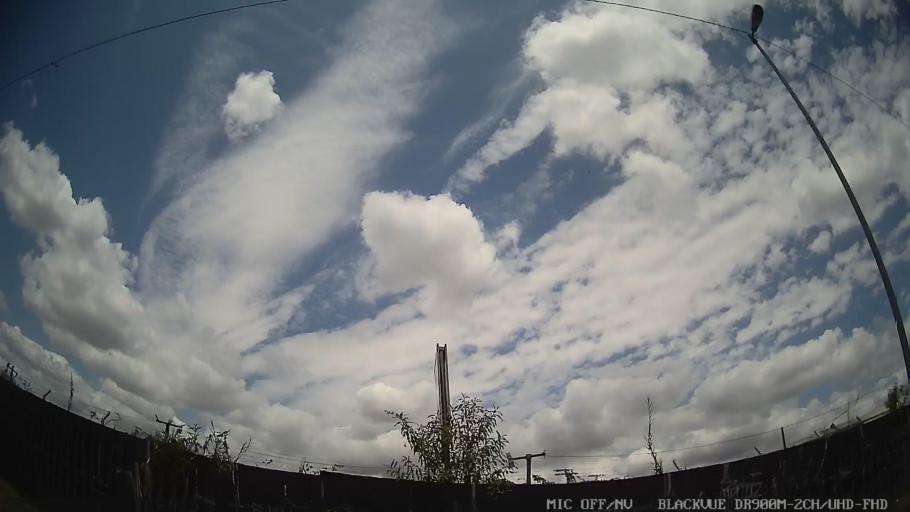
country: BR
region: Sao Paulo
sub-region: Guarulhos
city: Guarulhos
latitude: -23.5411
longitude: -46.4747
